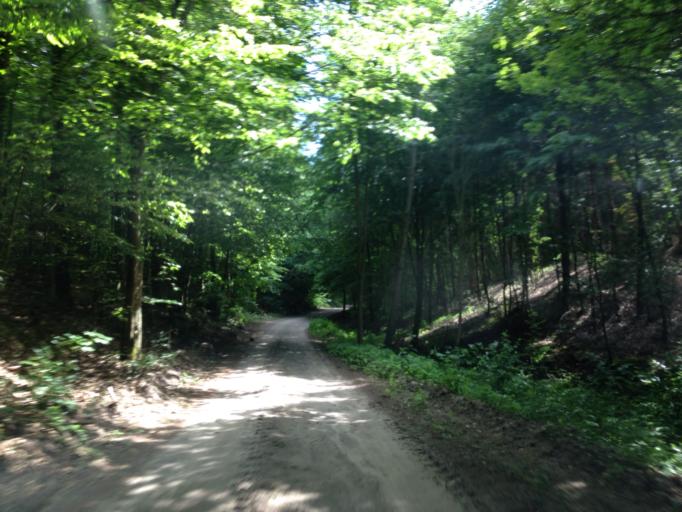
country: PL
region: Kujawsko-Pomorskie
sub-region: Powiat brodnicki
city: Gorzno
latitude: 53.2199
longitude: 19.6515
